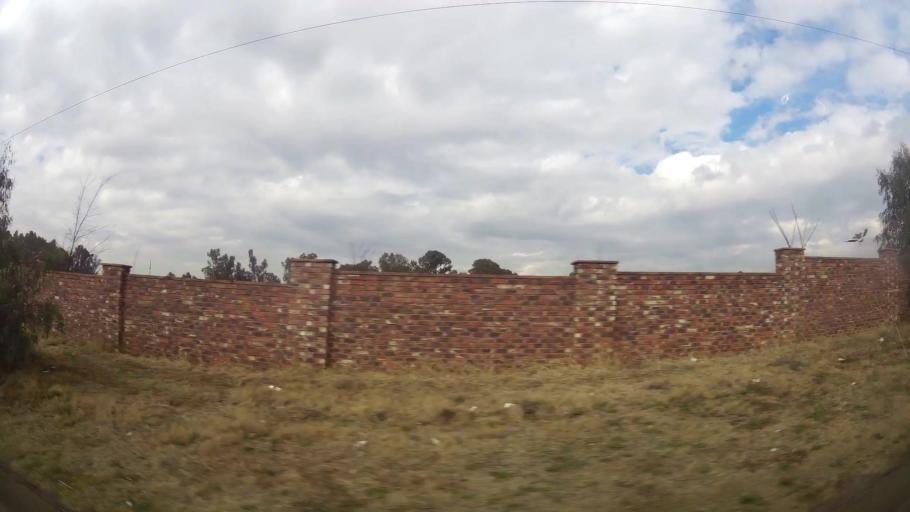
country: ZA
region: Gauteng
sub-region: Sedibeng District Municipality
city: Meyerton
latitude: -26.5879
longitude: 28.0068
